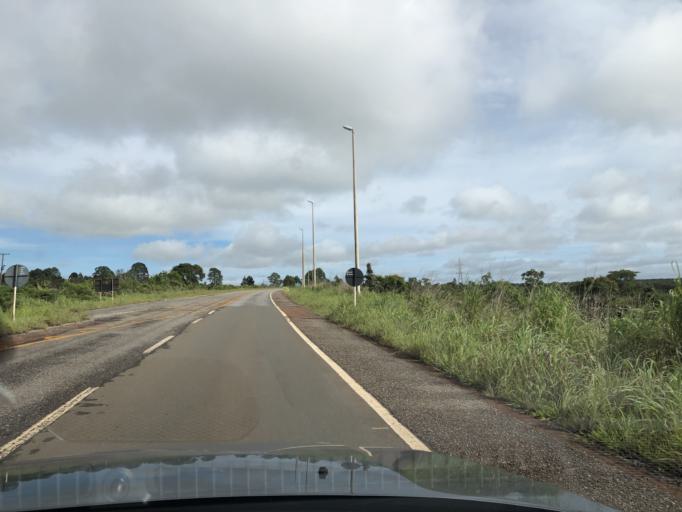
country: BR
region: Federal District
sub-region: Brasilia
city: Brasilia
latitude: -15.7288
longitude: -48.0844
